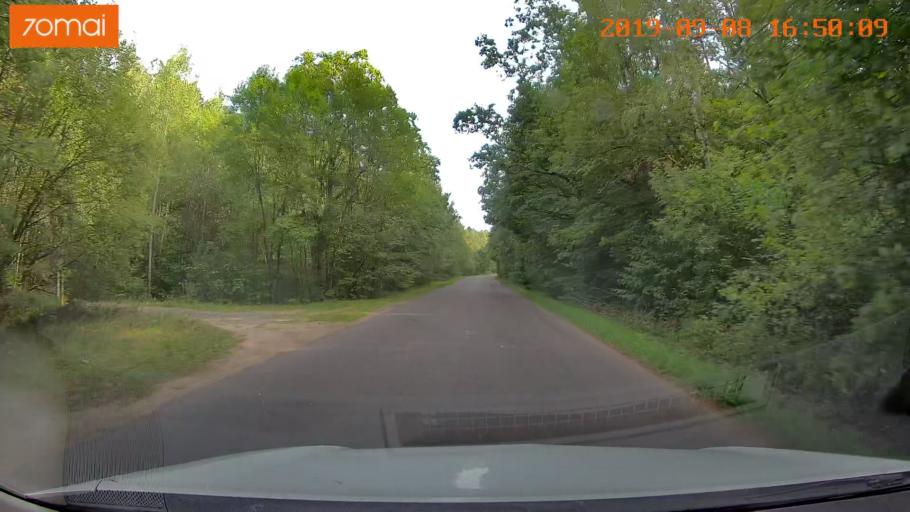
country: BY
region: Grodnenskaya
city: Hrodna
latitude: 53.8030
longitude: 23.8848
